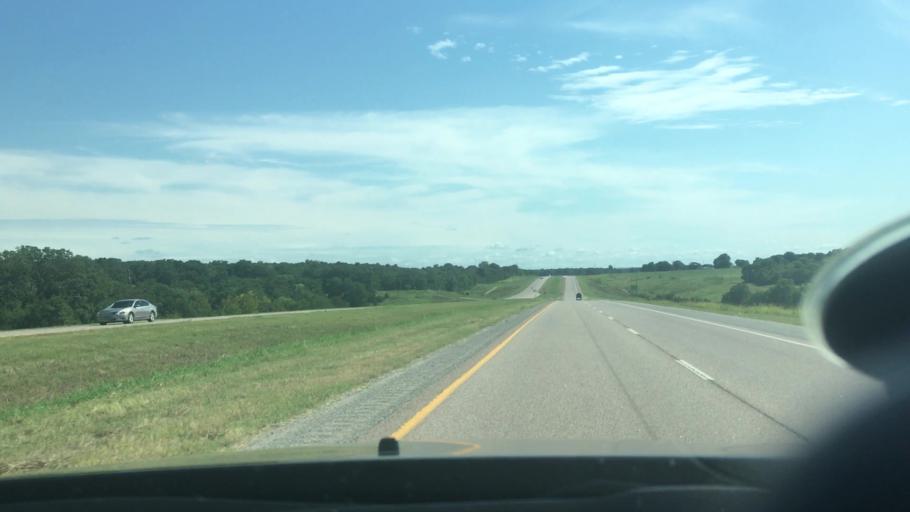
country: US
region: Oklahoma
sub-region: Pontotoc County
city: Byng
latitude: 34.8723
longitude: -96.6785
